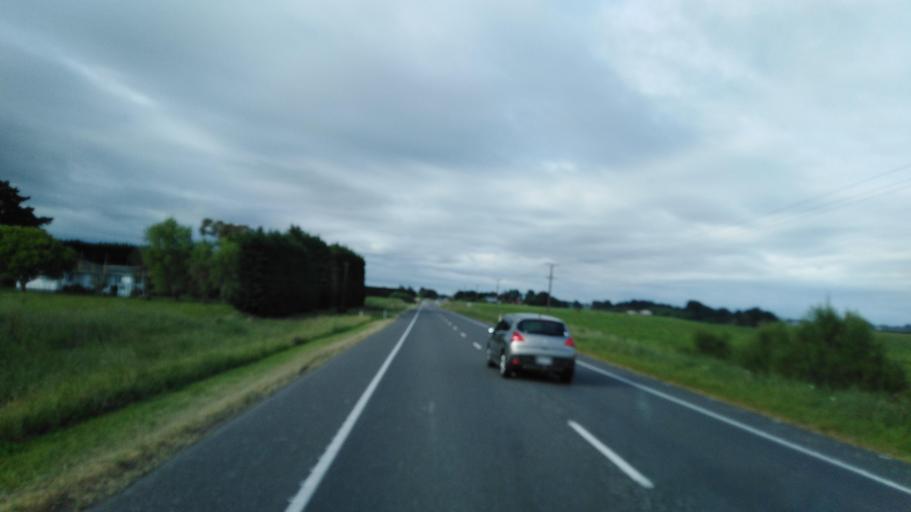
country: NZ
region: Manawatu-Wanganui
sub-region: Rangitikei District
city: Bulls
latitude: -40.2488
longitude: 175.3971
